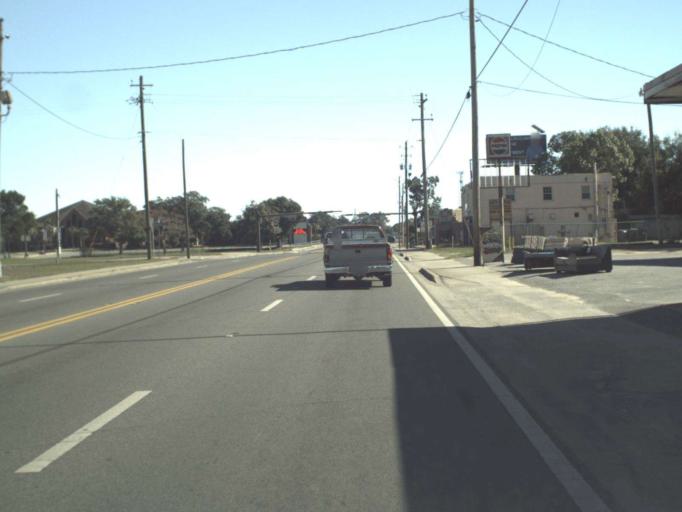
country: US
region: Florida
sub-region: Escambia County
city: West Pensacola
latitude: 30.4227
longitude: -87.2565
